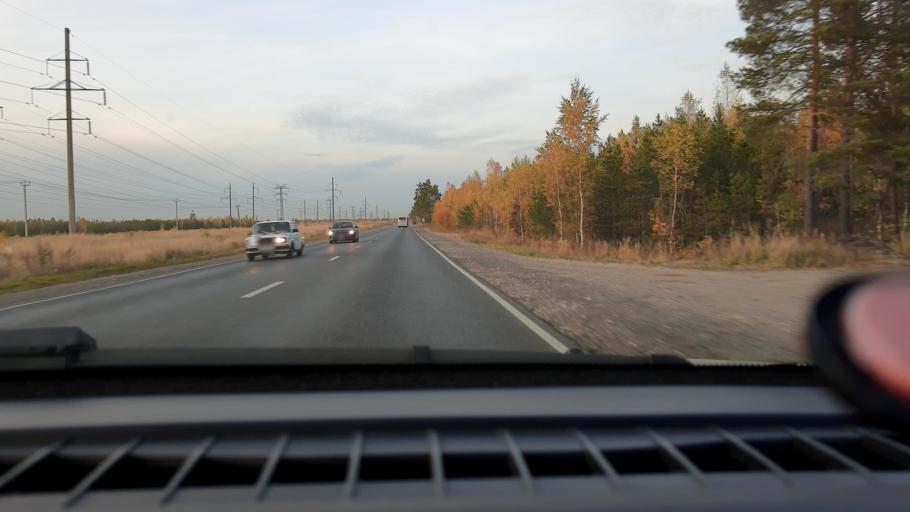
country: RU
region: Nizjnij Novgorod
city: Babino
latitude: 56.3147
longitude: 43.5591
